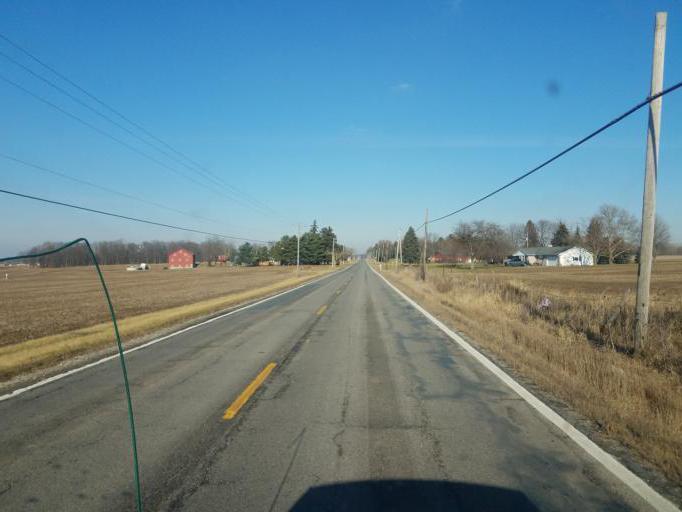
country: US
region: Ohio
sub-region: Marion County
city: Marion
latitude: 40.6317
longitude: -83.1282
